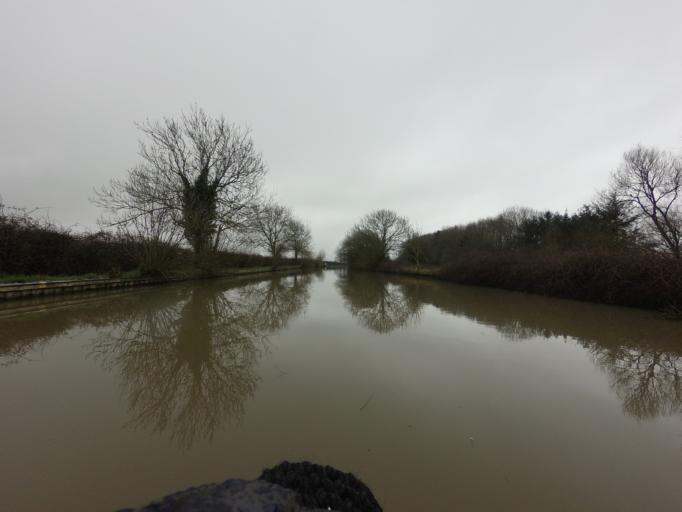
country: GB
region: England
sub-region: Milton Keynes
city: Castlethorpe
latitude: 52.0958
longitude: -0.8662
